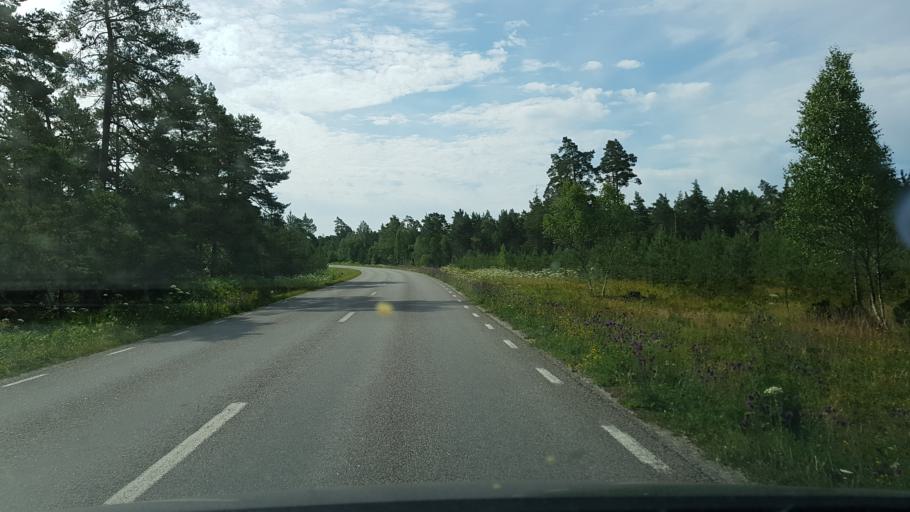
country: SE
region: Gotland
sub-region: Gotland
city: Hemse
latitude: 57.4547
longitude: 18.5784
